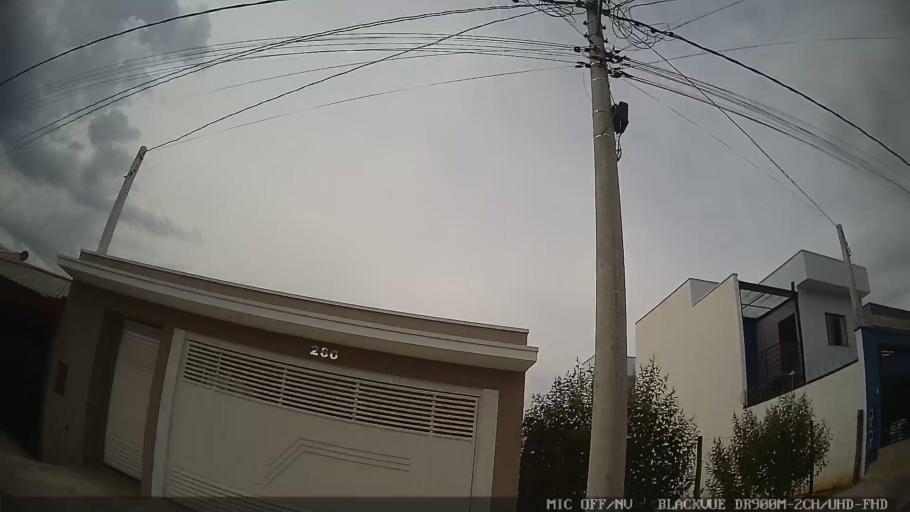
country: BR
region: Sao Paulo
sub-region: Indaiatuba
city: Indaiatuba
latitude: -23.0994
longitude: -47.2502
